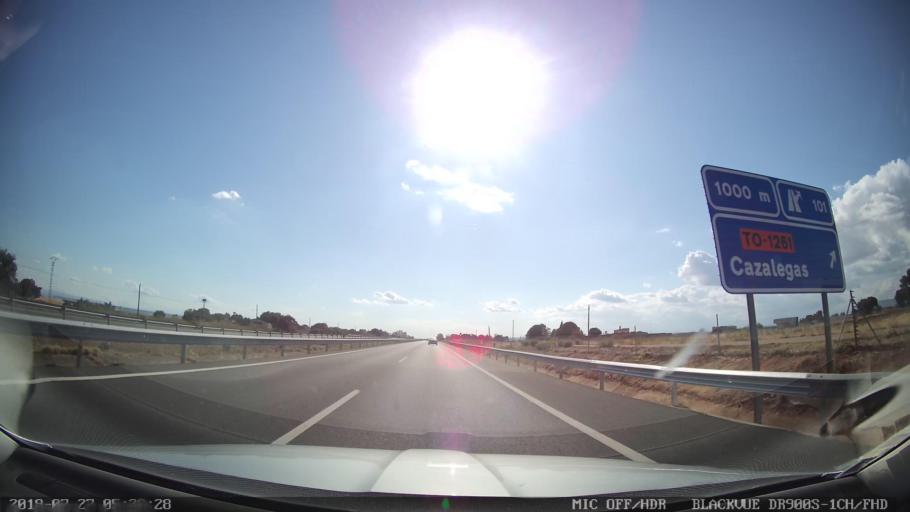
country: ES
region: Castille-La Mancha
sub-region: Province of Toledo
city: Cazalegas
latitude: 39.9992
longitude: -4.6594
